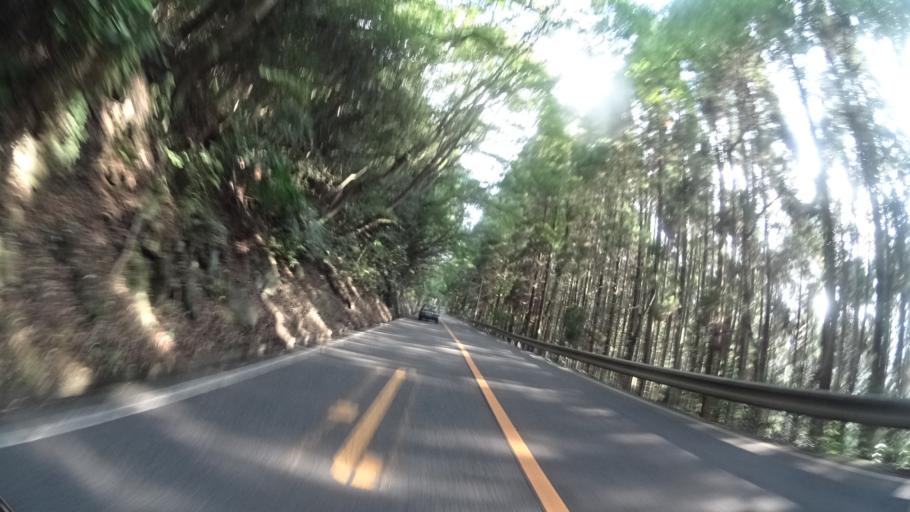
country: JP
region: Oita
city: Beppu
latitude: 33.2667
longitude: 131.3702
